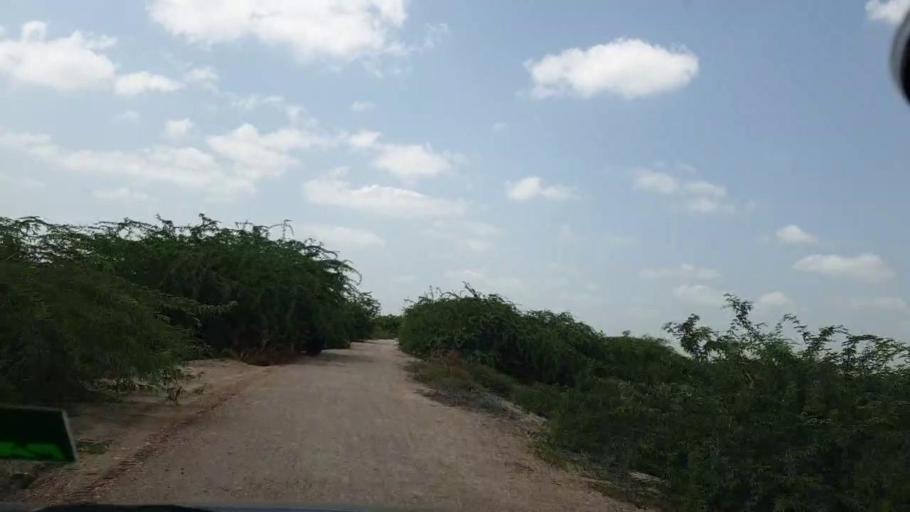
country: PK
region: Sindh
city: Kadhan
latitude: 24.5518
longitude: 69.1935
